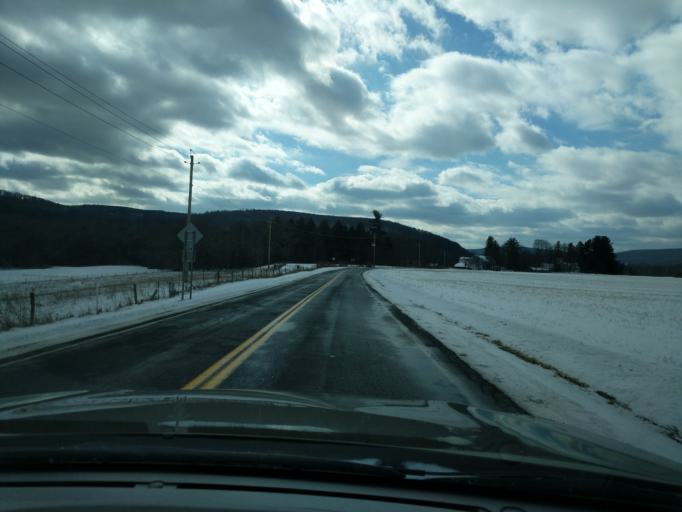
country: US
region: New York
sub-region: Tompkins County
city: East Ithaca
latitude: 42.3893
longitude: -76.3777
